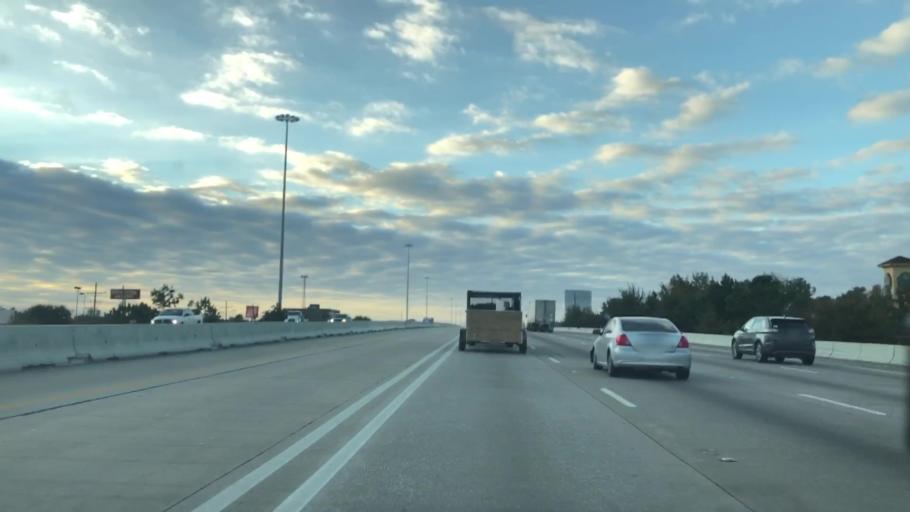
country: US
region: Texas
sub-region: Montgomery County
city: Shenandoah
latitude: 30.1814
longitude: -95.4523
